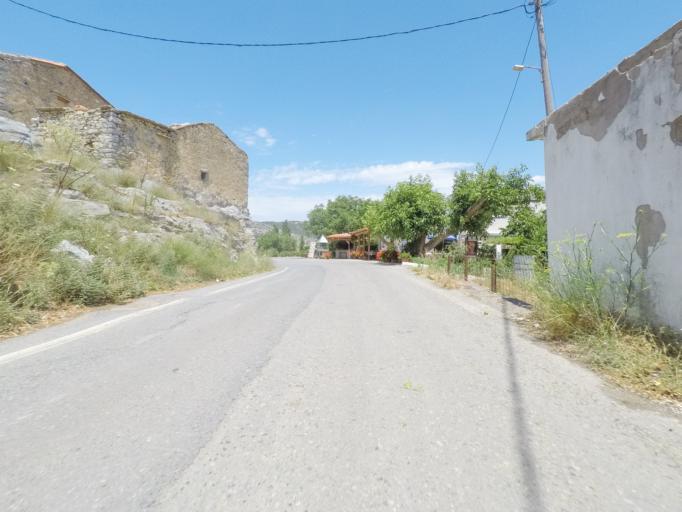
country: GR
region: Crete
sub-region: Nomos Irakleiou
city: Mokhos
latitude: 35.1853
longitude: 25.4322
